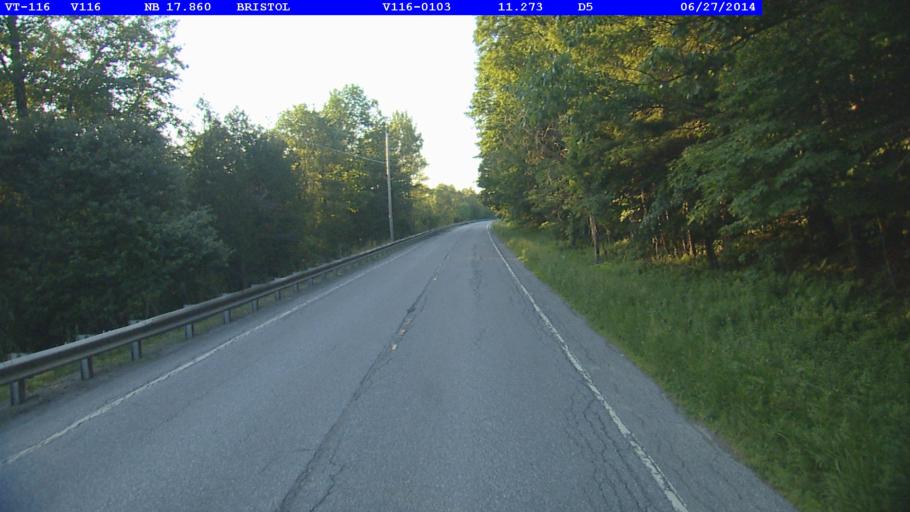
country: US
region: Vermont
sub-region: Addison County
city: Bristol
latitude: 44.1714
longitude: -73.0564
